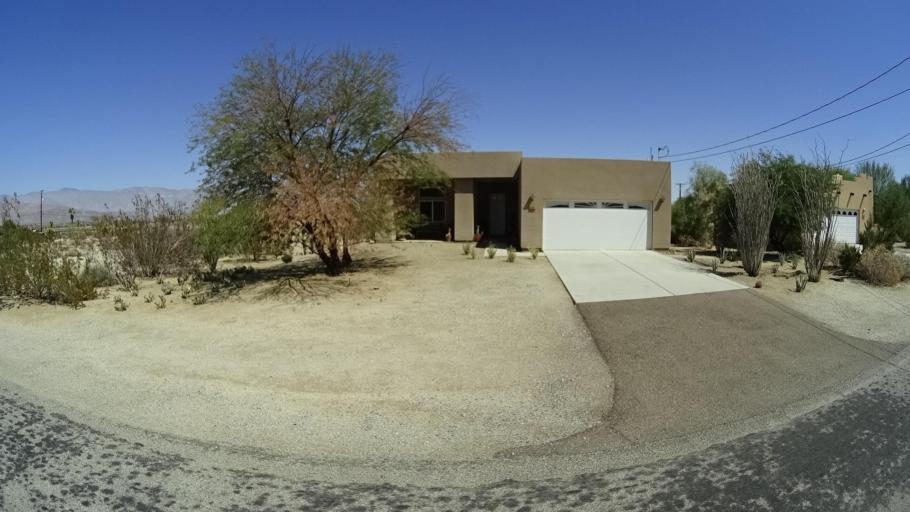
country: US
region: California
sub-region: San Diego County
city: Borrego Springs
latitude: 33.2265
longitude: -116.3673
